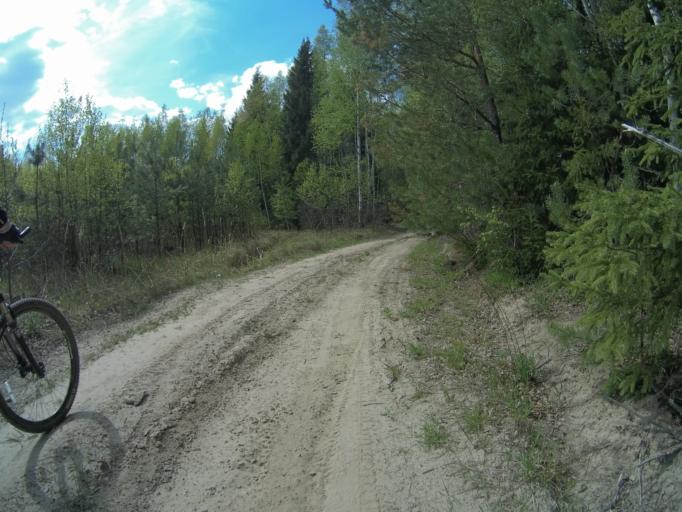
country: RU
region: Vladimir
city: Raduzhnyy
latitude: 55.9667
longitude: 40.2234
